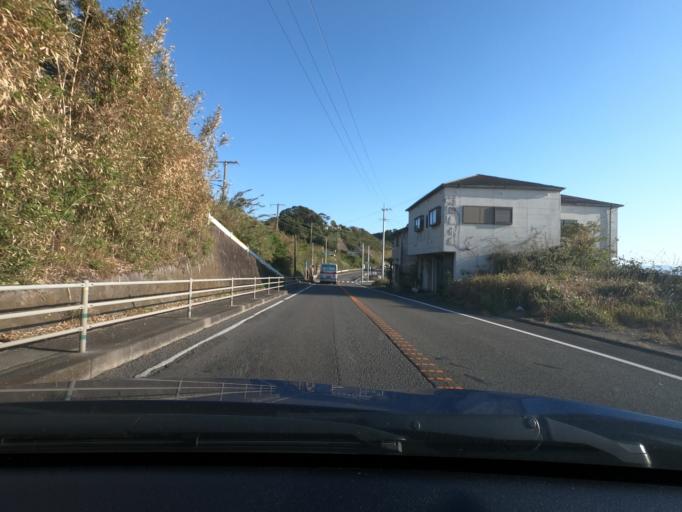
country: JP
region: Kagoshima
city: Akune
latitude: 31.9724
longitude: 130.2092
